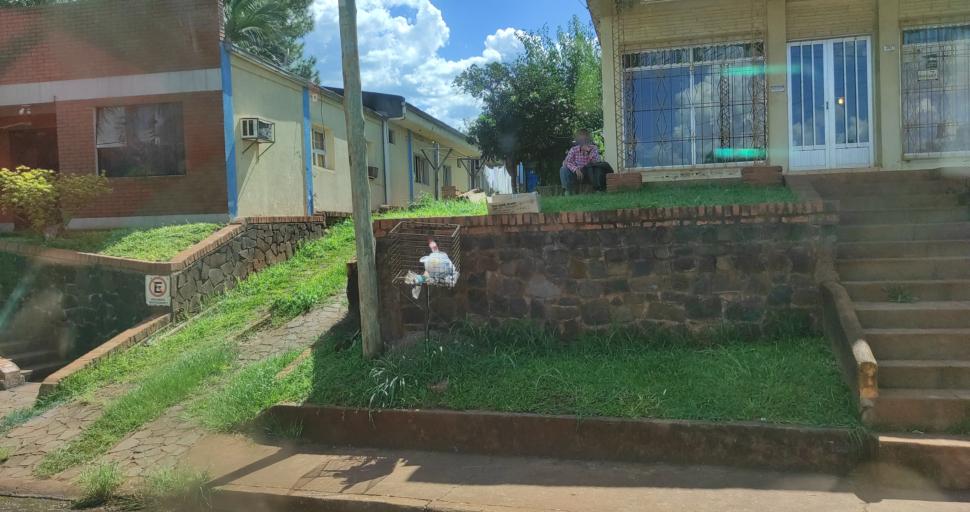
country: AR
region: Misiones
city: El Soberbio
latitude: -27.2941
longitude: -54.1984
